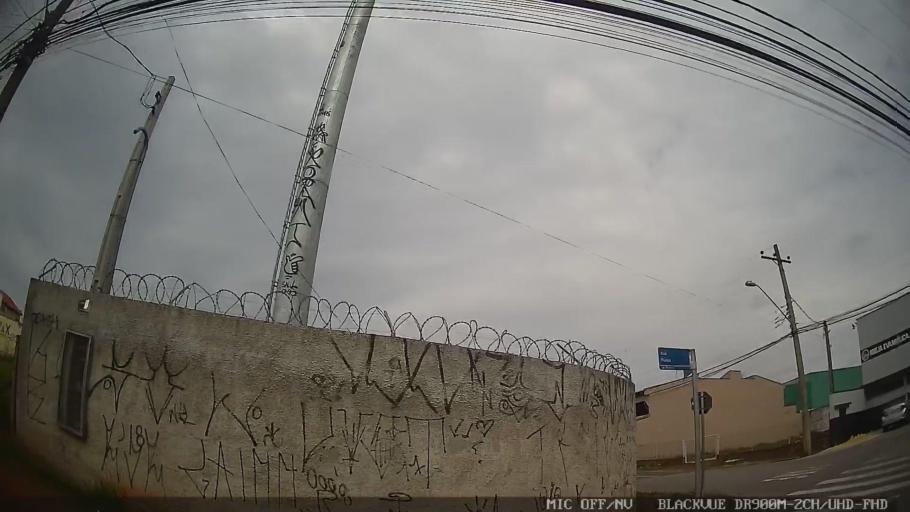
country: BR
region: Sao Paulo
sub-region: Salto
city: Salto
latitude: -23.1901
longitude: -47.2779
